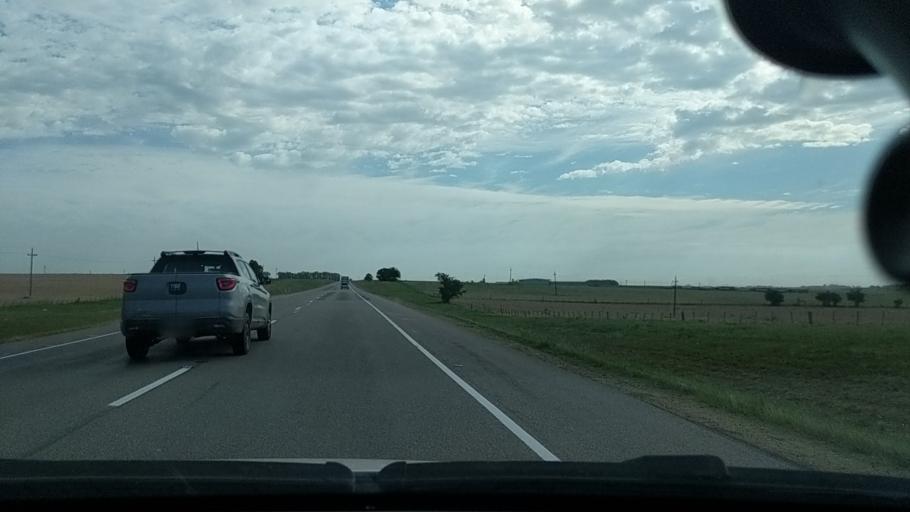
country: UY
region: Florida
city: Cardal
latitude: -34.3117
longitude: -56.2376
